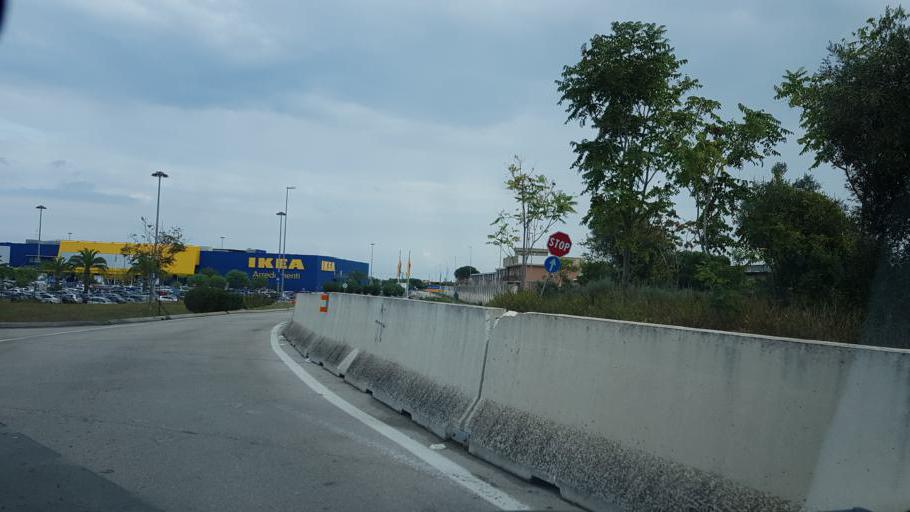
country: IT
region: Apulia
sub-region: Provincia di Bari
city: Triggiano
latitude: 41.0862
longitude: 16.8964
